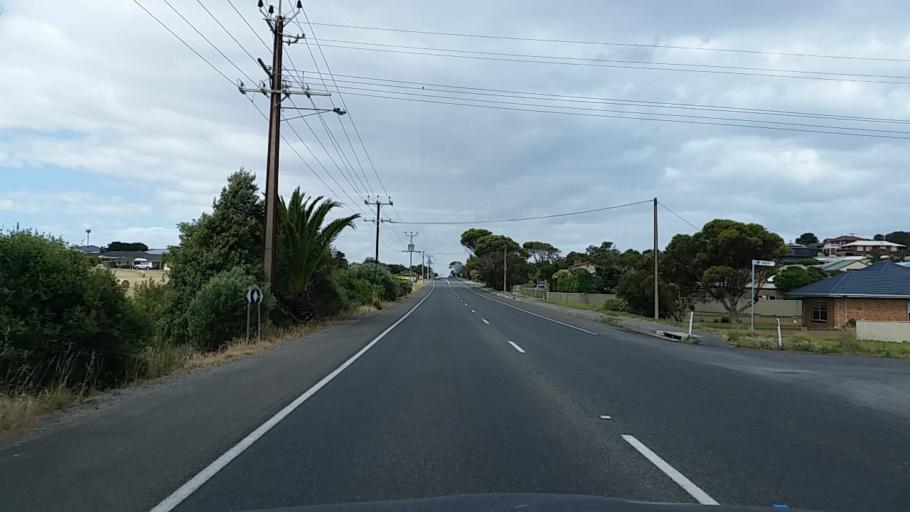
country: AU
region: South Australia
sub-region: Alexandrina
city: Port Elliot
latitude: -35.5321
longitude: 138.6684
